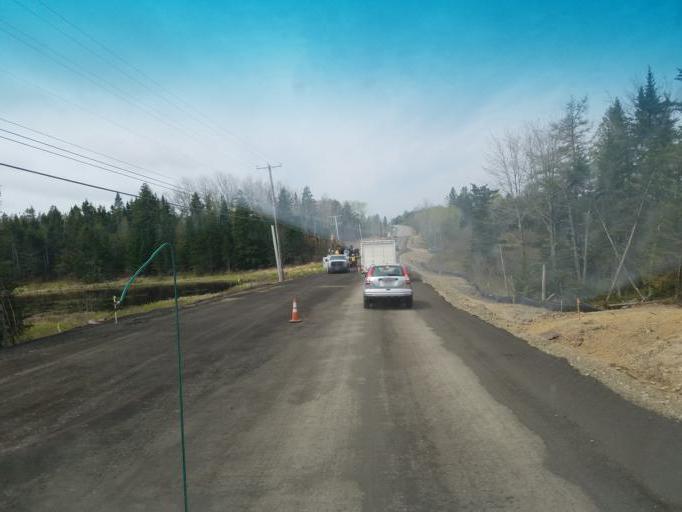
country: US
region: Maine
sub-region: Washington County
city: East Machias
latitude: 44.7660
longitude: -67.2014
